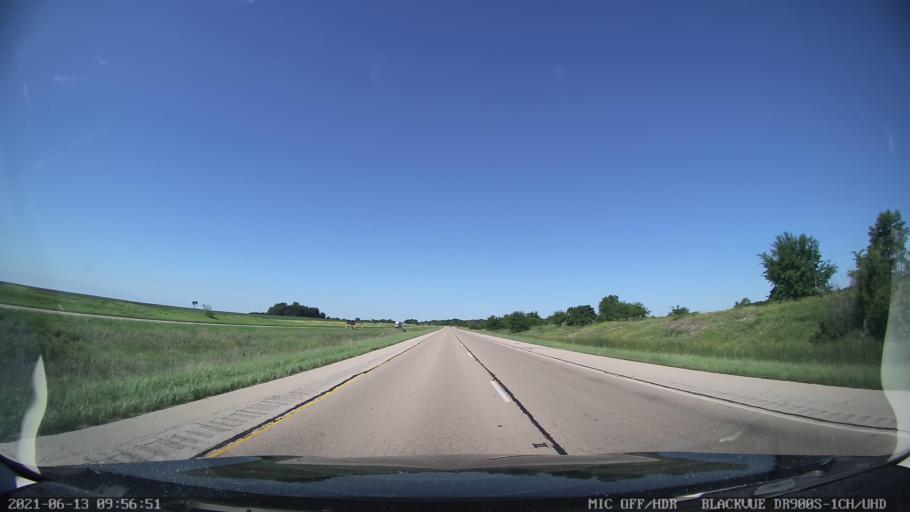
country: US
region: Illinois
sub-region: Logan County
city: Atlanta
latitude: 40.3506
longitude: -89.1211
